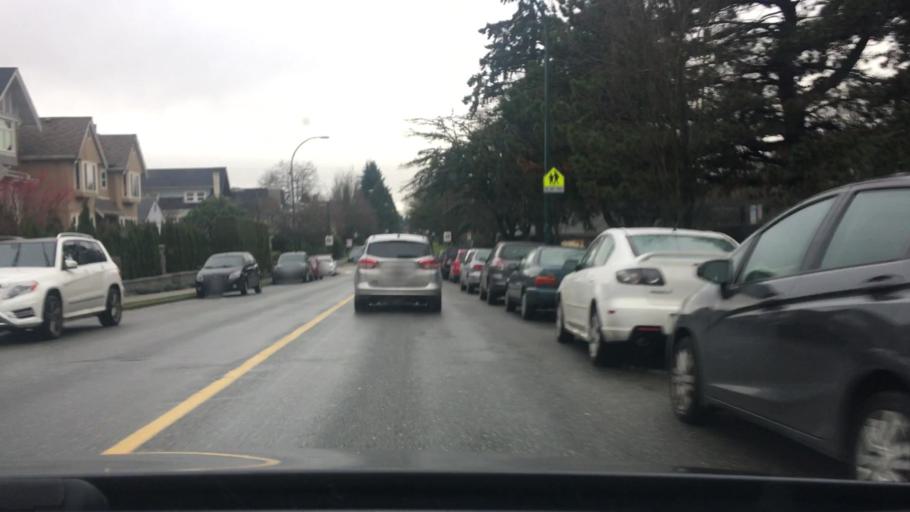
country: CA
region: British Columbia
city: Vancouver
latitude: 49.2567
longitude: -123.1059
